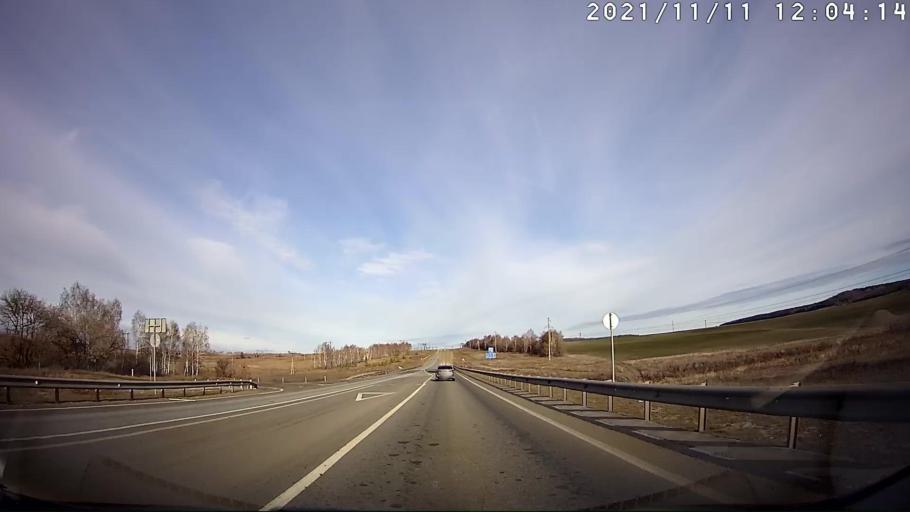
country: RU
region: Ulyanovsk
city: Silikatnyy
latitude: 53.6523
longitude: 48.3486
